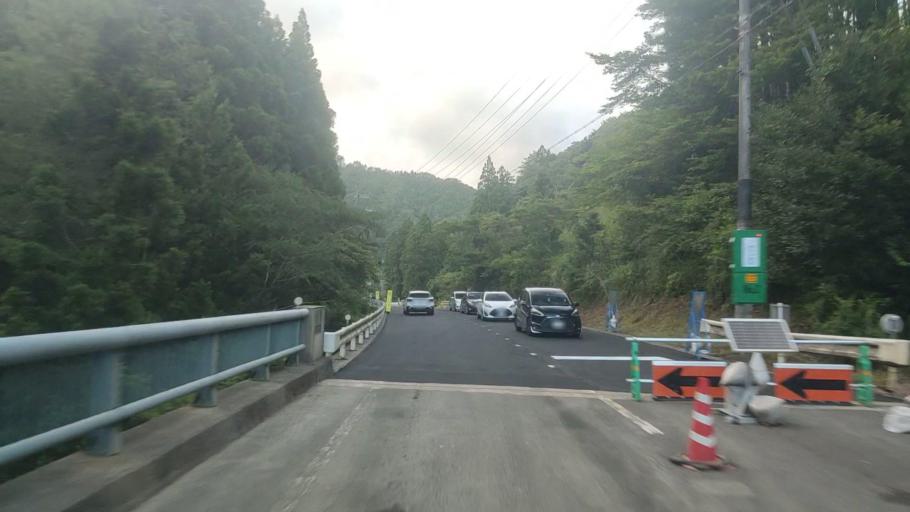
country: JP
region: Wakayama
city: Tanabe
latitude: 33.8316
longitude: 135.6513
